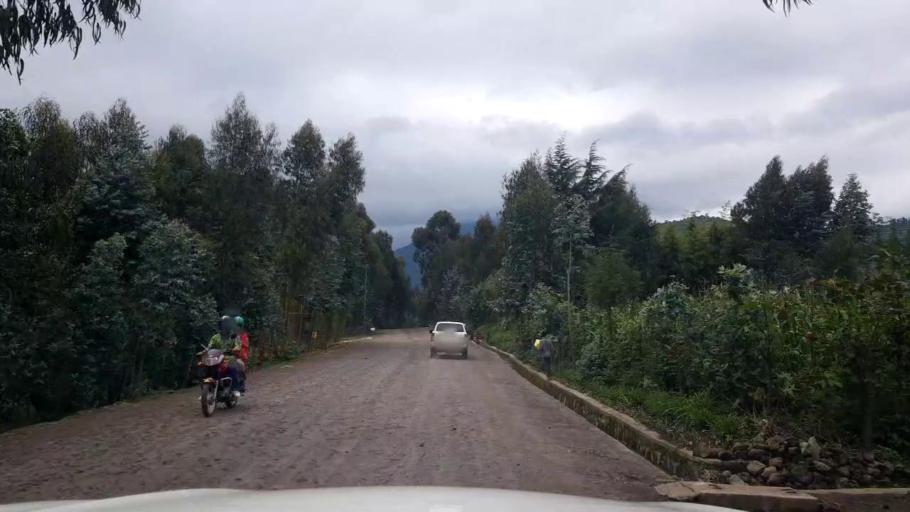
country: RW
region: Northern Province
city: Musanze
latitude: -1.4419
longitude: 29.5390
